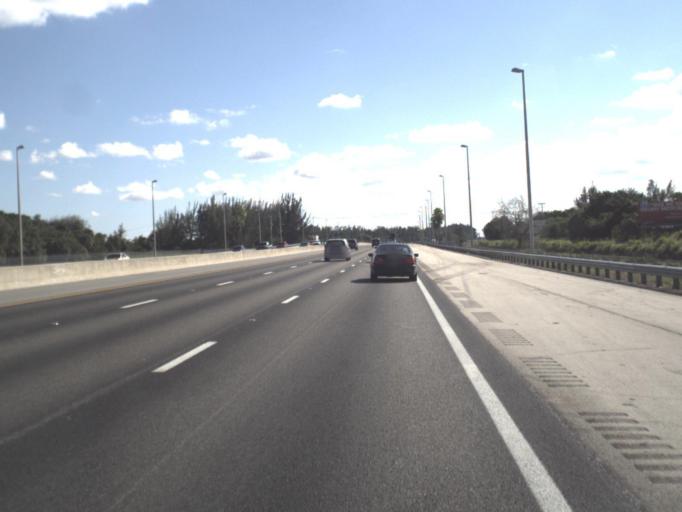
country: US
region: Florida
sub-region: Palm Beach County
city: Villages of Oriole
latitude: 26.4873
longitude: -80.1727
